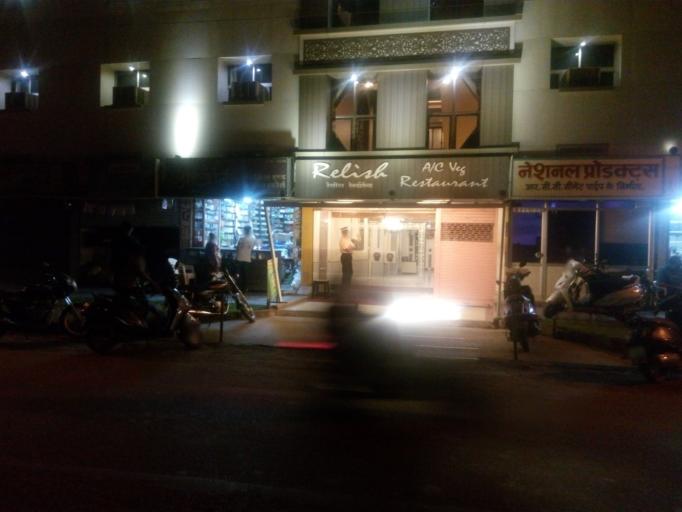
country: IN
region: Maharashtra
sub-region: Gondiya
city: Gondia
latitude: 21.4637
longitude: 80.1937
